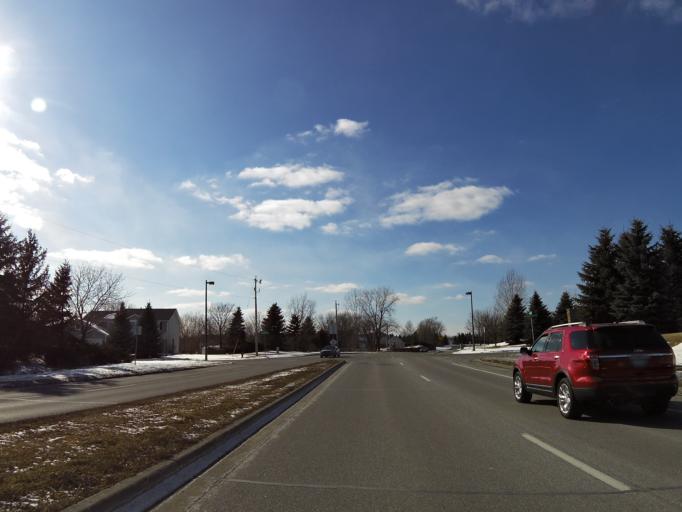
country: US
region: Minnesota
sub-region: Washington County
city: Woodbury
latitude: 44.9053
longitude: -92.9469
